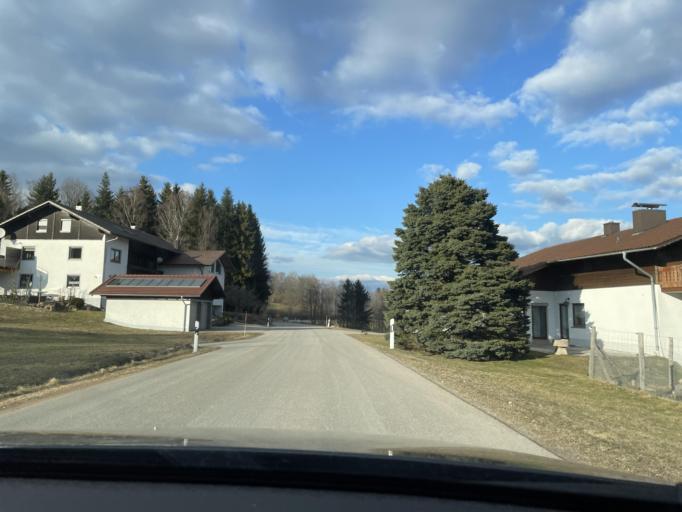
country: DE
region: Bavaria
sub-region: Lower Bavaria
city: Kollnburg
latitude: 49.0288
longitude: 12.8626
